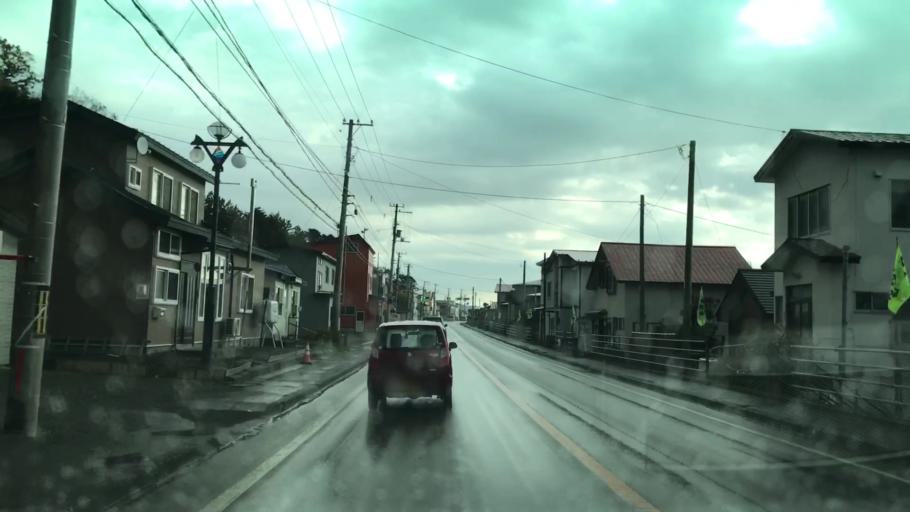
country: JP
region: Hokkaido
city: Shizunai-furukawacho
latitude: 42.1783
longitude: 142.7330
